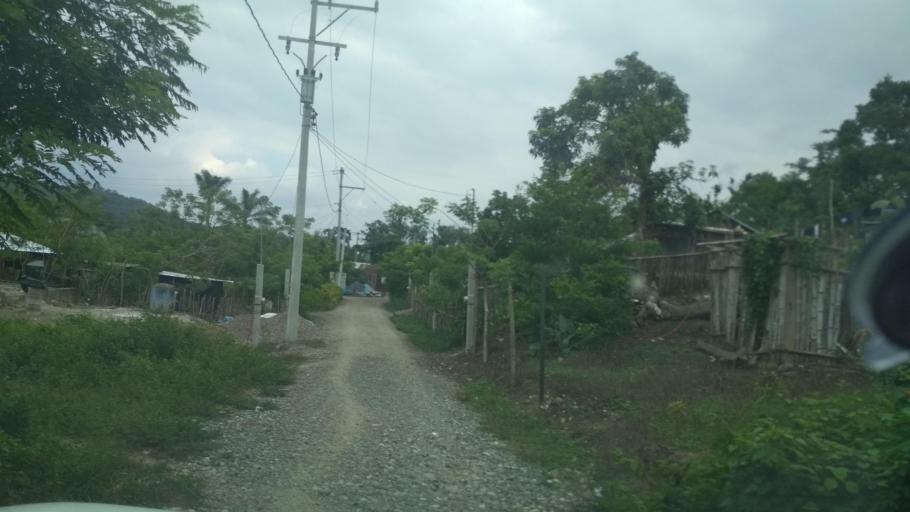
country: MX
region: Veracruz
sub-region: Poza Rica de Hidalgo
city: El Mollejon
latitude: 20.5339
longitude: -97.3891
